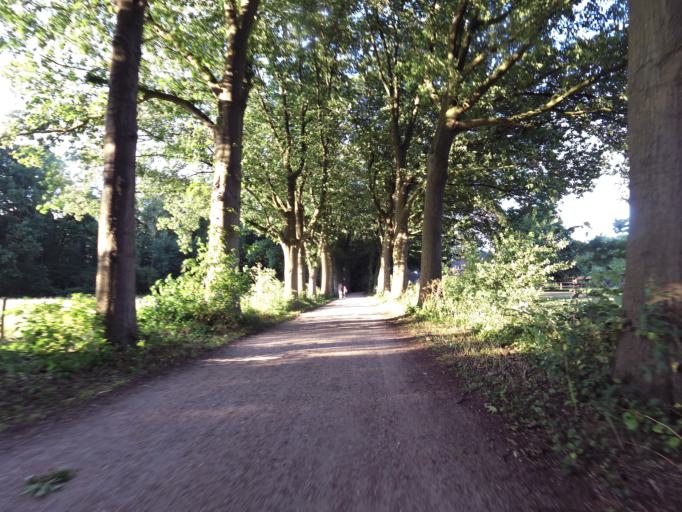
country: NL
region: Gelderland
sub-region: Gemeente Doetinchem
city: Doetinchem
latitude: 51.9793
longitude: 6.2860
